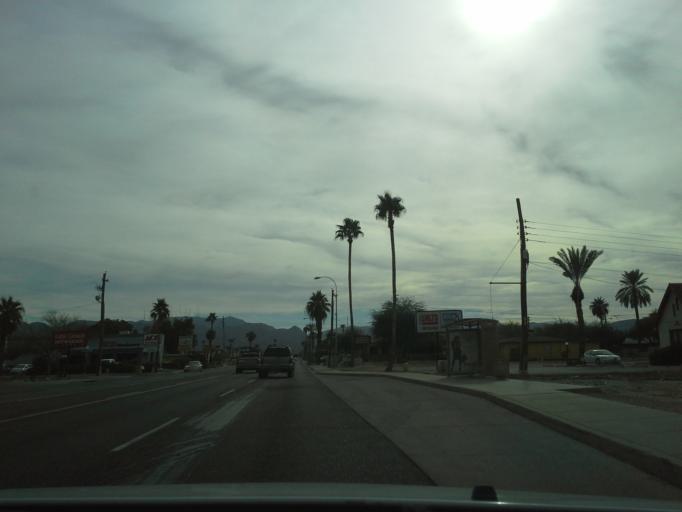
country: US
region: Arizona
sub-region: Maricopa County
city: Phoenix
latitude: 33.3849
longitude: -112.0734
